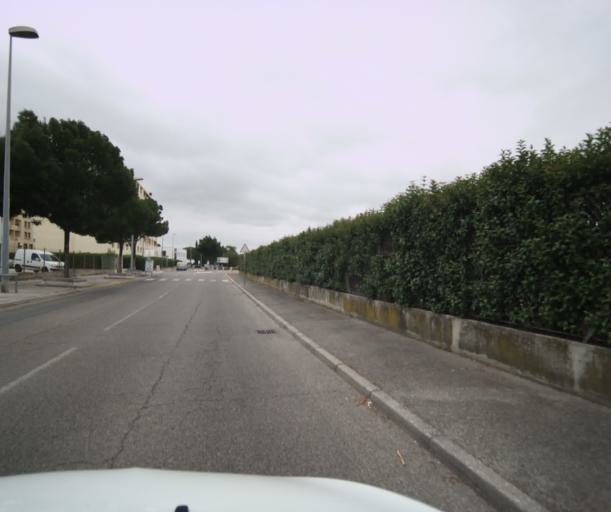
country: FR
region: Provence-Alpes-Cote d'Azur
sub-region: Departement du Var
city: La Valette-du-Var
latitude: 43.1357
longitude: 5.9944
